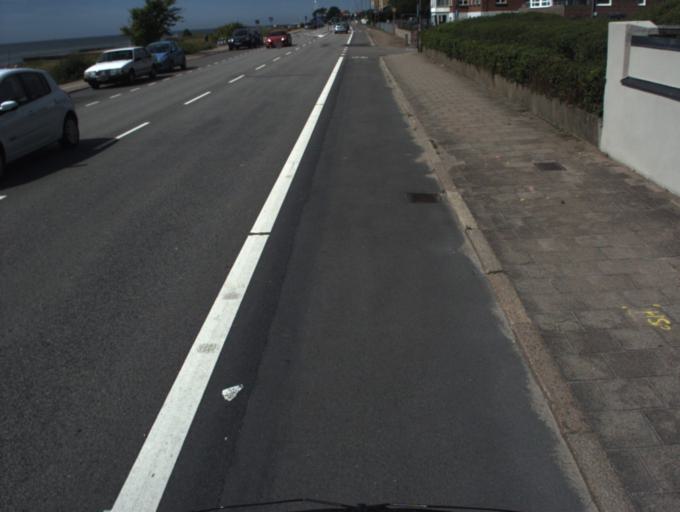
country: SE
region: Skane
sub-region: Helsingborg
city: Helsingborg
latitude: 56.0691
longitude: 12.6734
